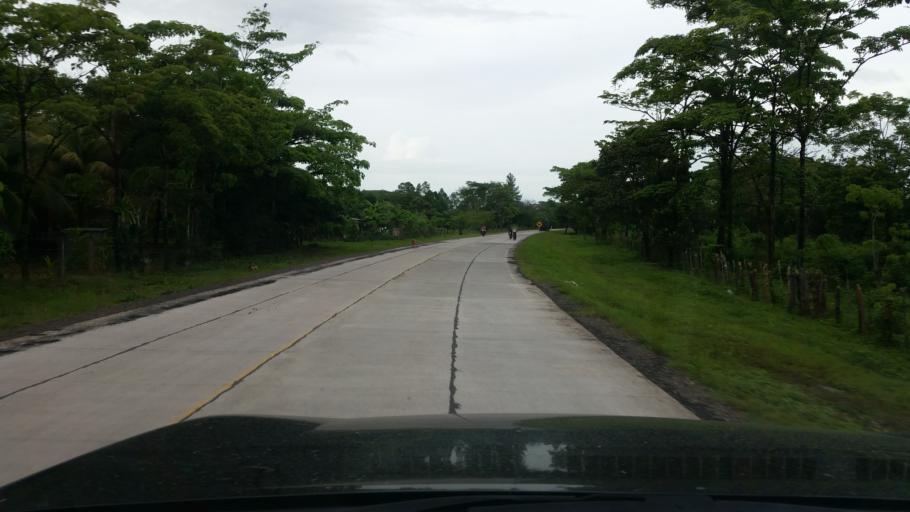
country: NI
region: Matagalpa
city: Rio Blanco
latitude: 13.1537
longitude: -84.9797
